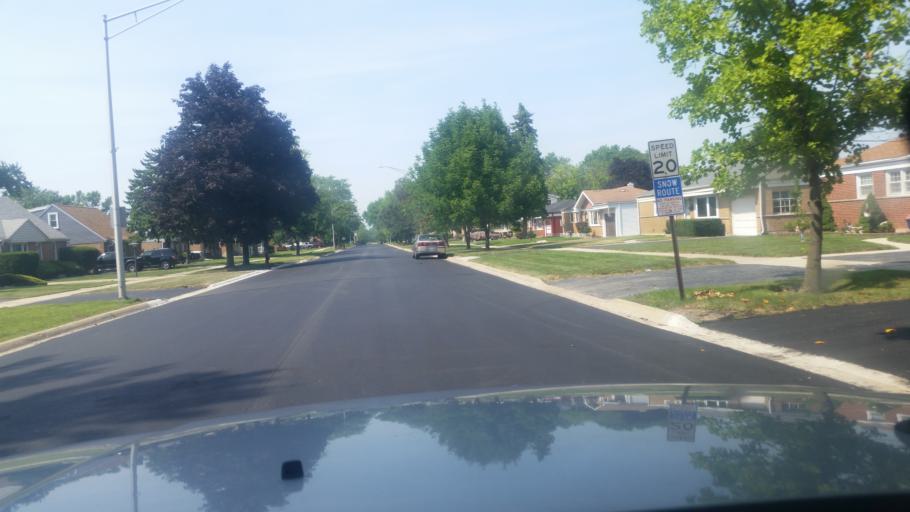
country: US
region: Illinois
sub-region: Cook County
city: Chicago Ridge
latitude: 41.6944
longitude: -87.7692
